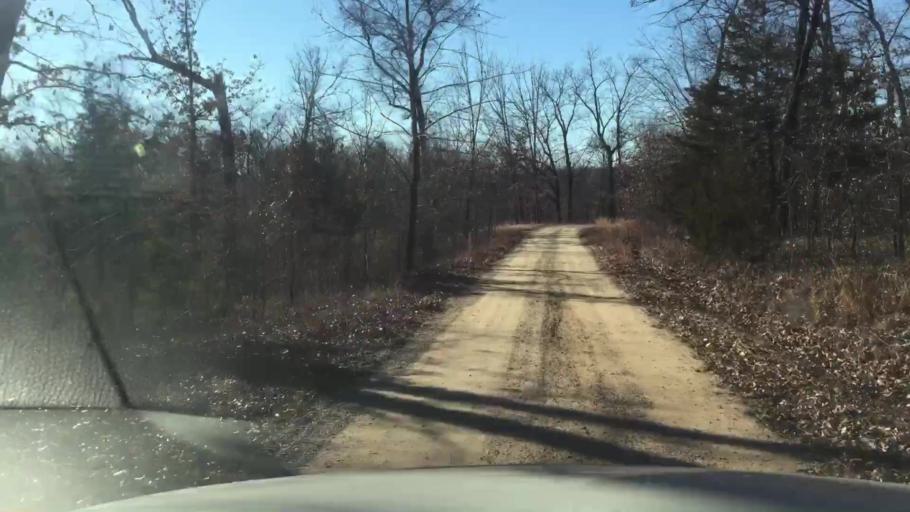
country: US
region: Missouri
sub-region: Camden County
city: Four Seasons
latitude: 38.3197
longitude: -92.7581
